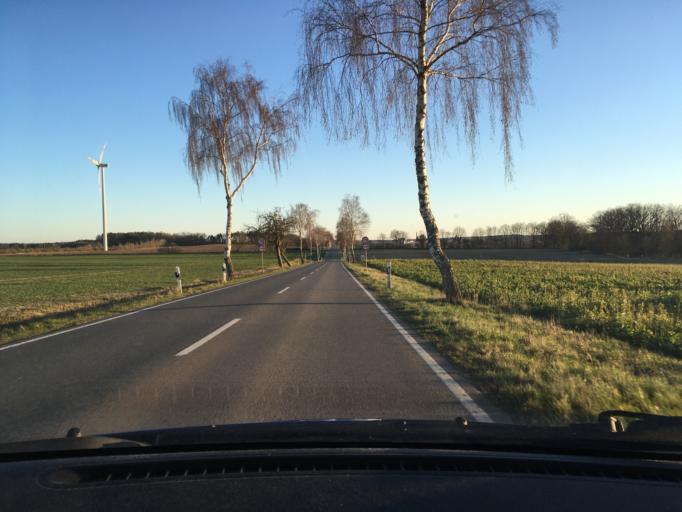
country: DE
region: Lower Saxony
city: Dahlem
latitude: 53.2066
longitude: 10.7522
